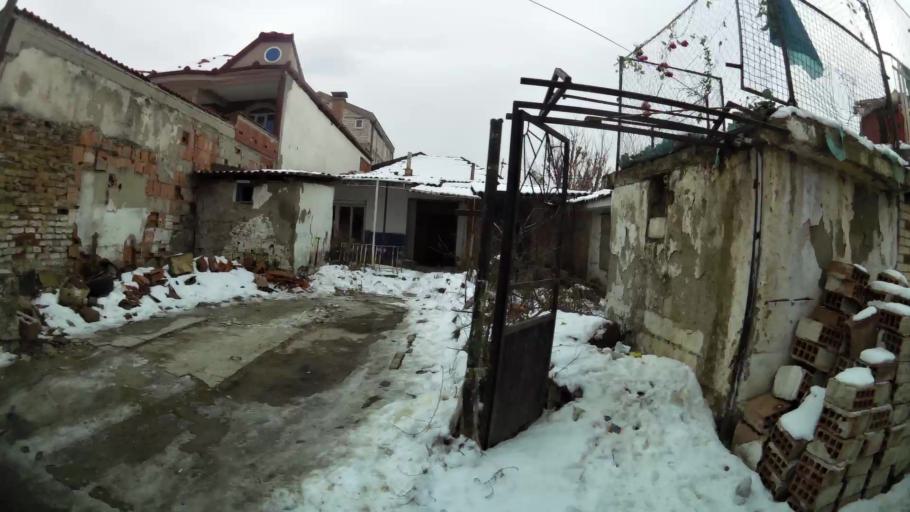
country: MK
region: Suto Orizari
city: Suto Orizare
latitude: 42.0405
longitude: 21.4213
